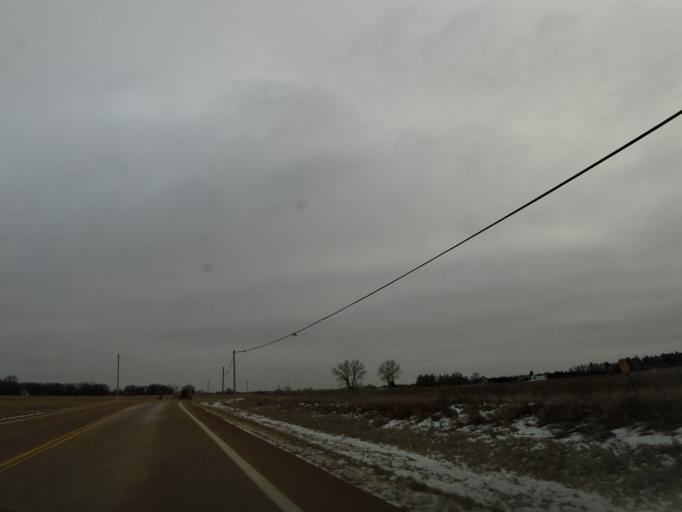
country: US
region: Minnesota
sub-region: Carver County
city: Carver
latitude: 44.7379
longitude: -93.6495
